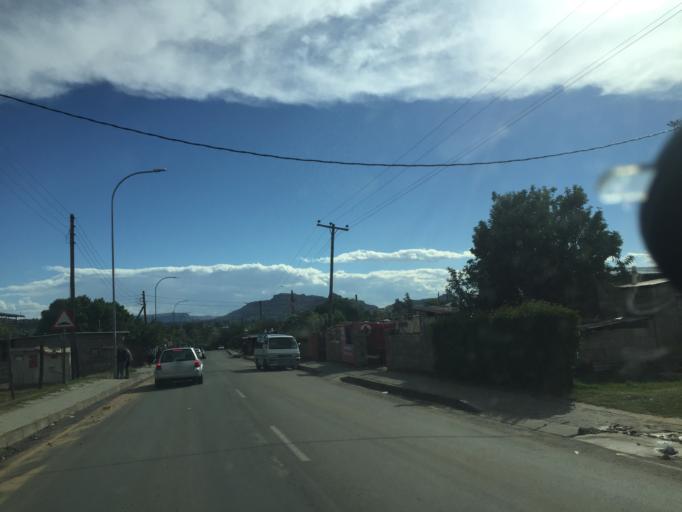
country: LS
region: Maseru
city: Maseru
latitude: -29.3055
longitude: 27.5327
